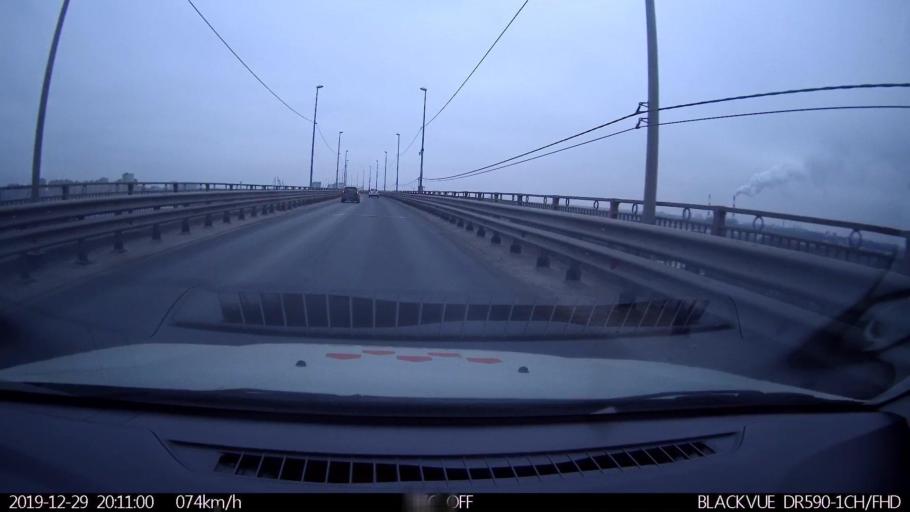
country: RU
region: Nizjnij Novgorod
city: Neklyudovo
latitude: 56.3605
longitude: 43.9297
